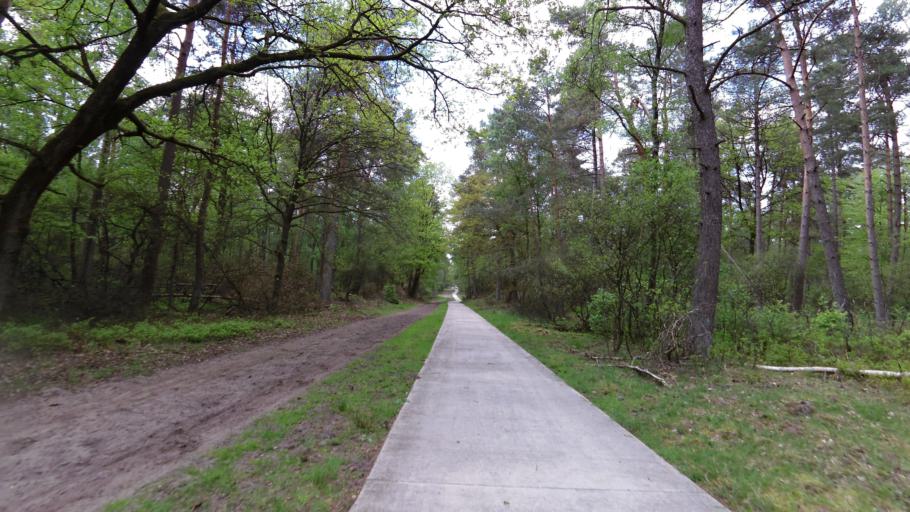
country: NL
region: Gelderland
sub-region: Gemeente Brummen
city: Eerbeek
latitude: 52.0696
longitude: 6.0630
